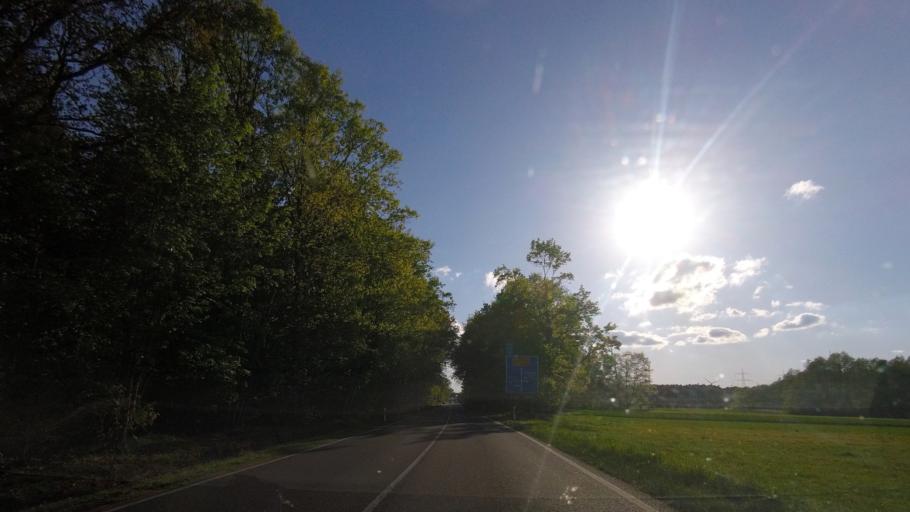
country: DE
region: Brandenburg
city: Luebben
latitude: 51.9014
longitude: 13.8214
